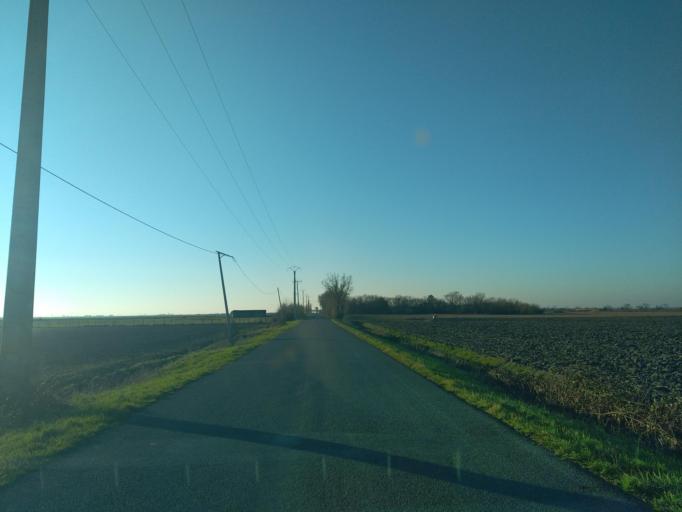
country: FR
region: Pays de la Loire
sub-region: Departement de la Vendee
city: Triaize
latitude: 46.3879
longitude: -1.2685
